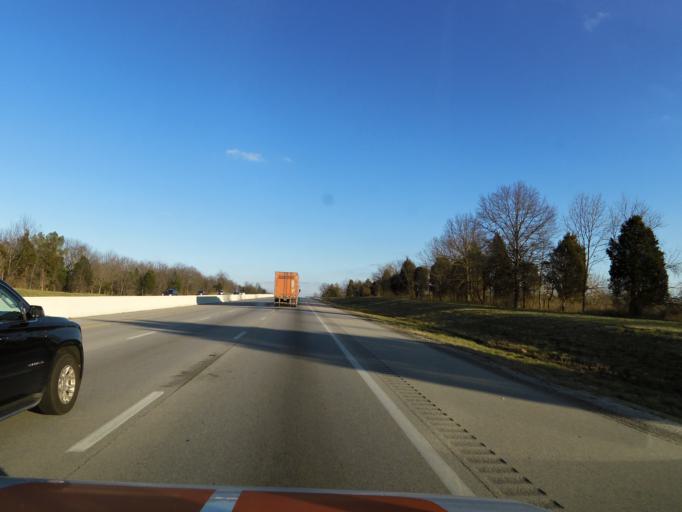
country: US
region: Kentucky
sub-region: Shelby County
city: Simpsonville
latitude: 38.2167
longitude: -85.4019
